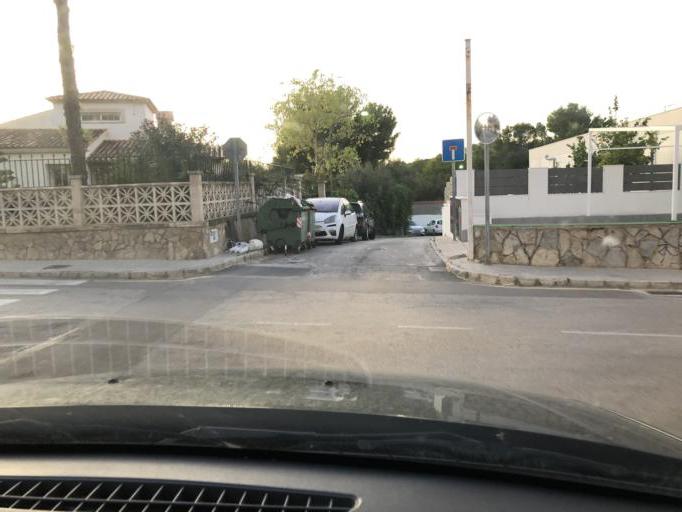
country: ES
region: Balearic Islands
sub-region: Illes Balears
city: Santa Ponsa
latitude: 39.5228
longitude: 2.4738
